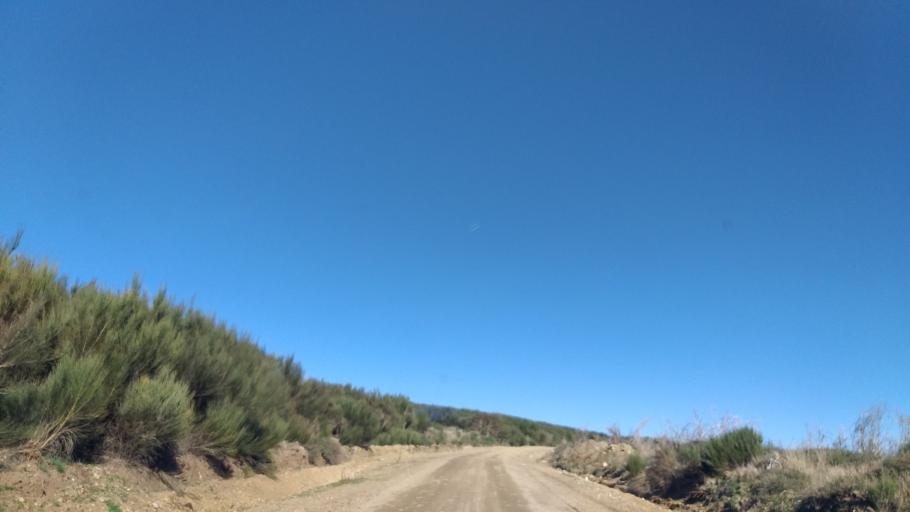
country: PT
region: Guarda
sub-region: Manteigas
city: Manteigas
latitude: 40.5042
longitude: -7.4858
